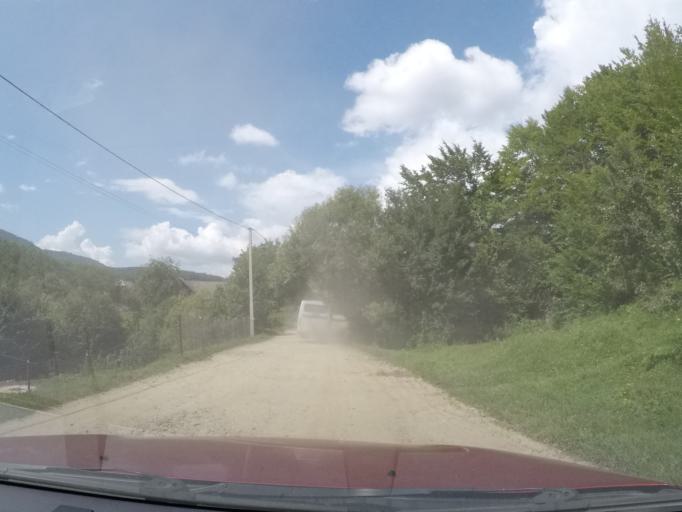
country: UA
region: Zakarpattia
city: Velykyi Bereznyi
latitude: 49.0274
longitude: 22.5970
